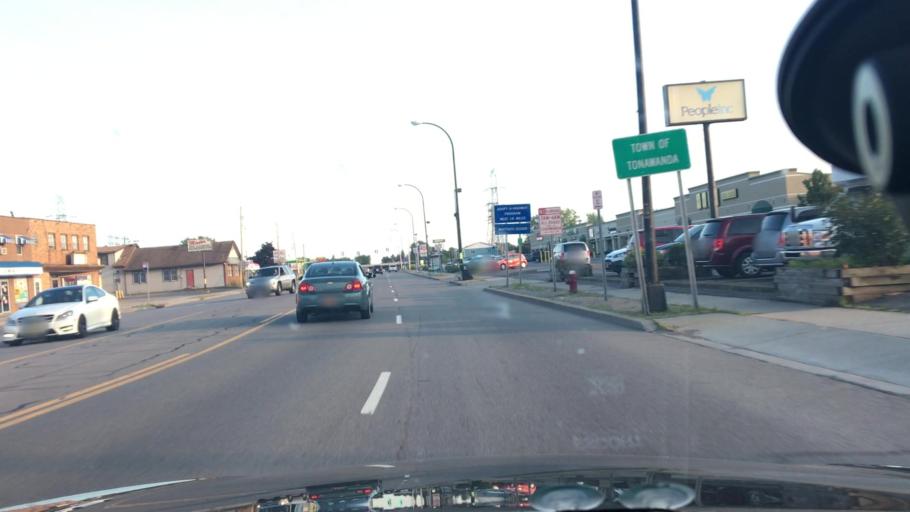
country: US
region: New York
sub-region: Erie County
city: Tonawanda
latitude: 43.0012
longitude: -78.8753
